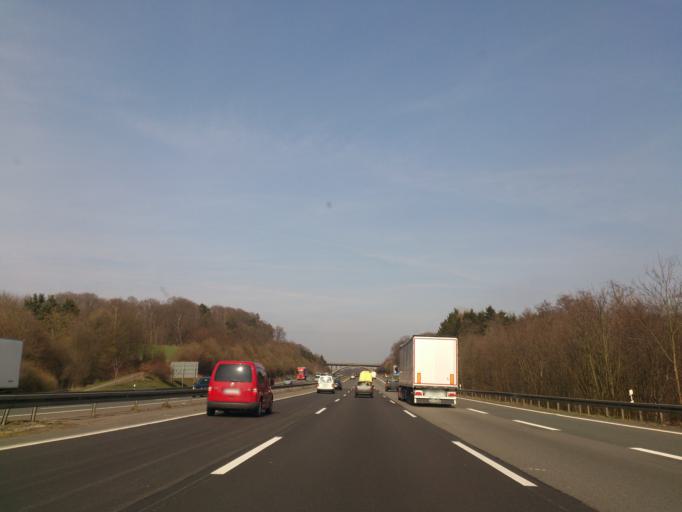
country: DE
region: North Rhine-Westphalia
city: Gevelsberg
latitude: 51.3406
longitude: 7.3352
